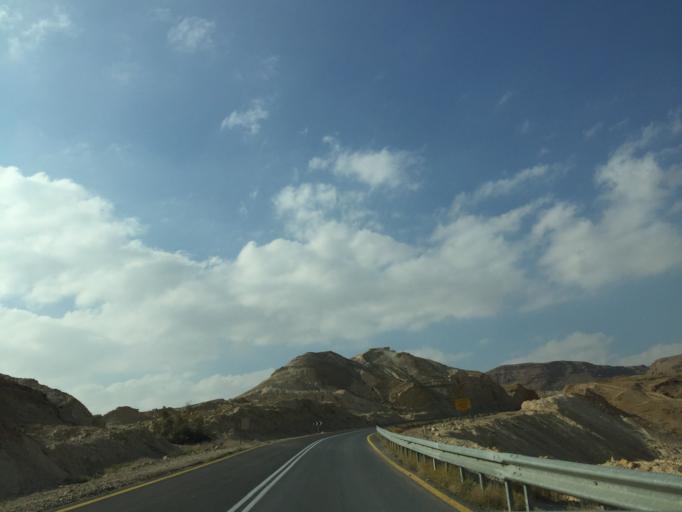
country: IL
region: Southern District
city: `En Boqeq
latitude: 31.3170
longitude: 35.3468
